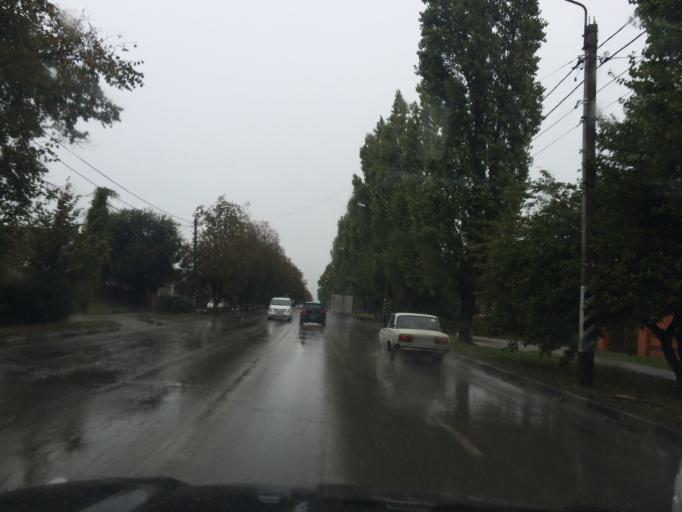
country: RU
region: Rostov
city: Azov
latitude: 47.0959
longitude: 39.4461
